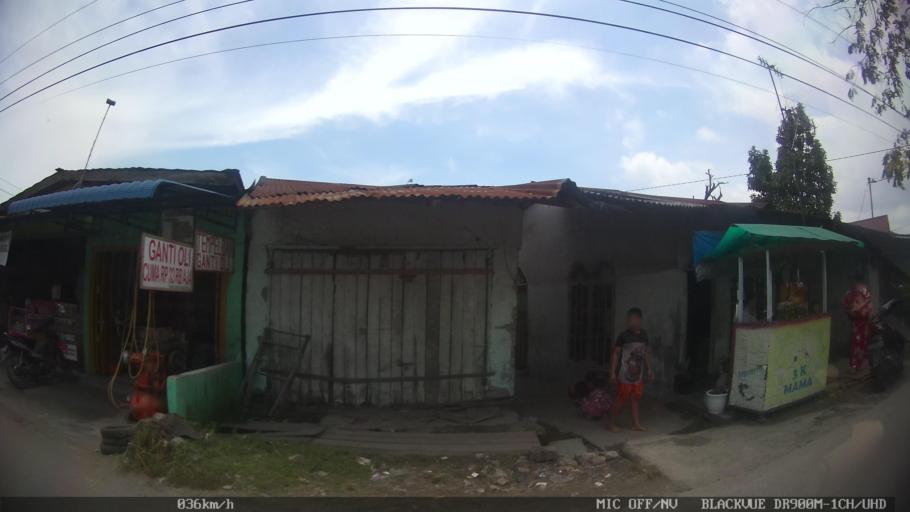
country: ID
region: North Sumatra
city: Labuhan Deli
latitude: 3.6826
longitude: 98.6890
